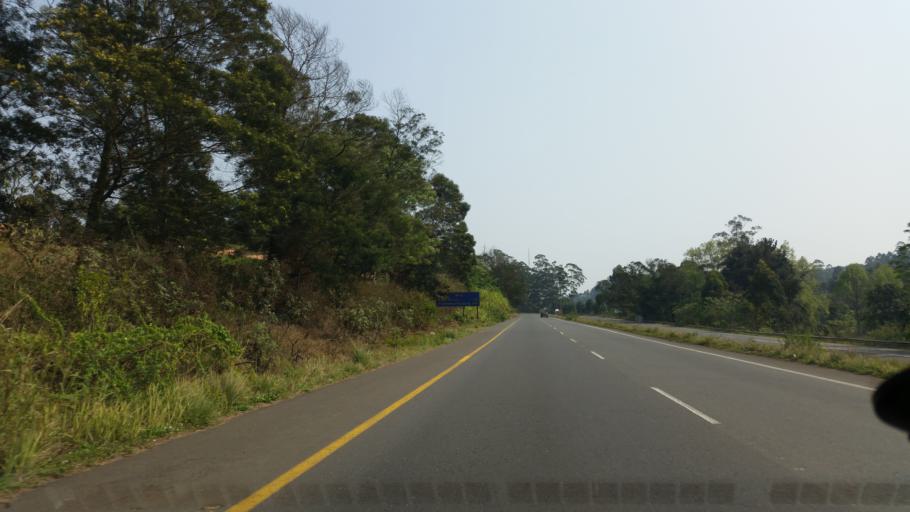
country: ZA
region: KwaZulu-Natal
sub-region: eThekwini Metropolitan Municipality
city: Mpumalanga
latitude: -29.7912
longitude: 30.7370
